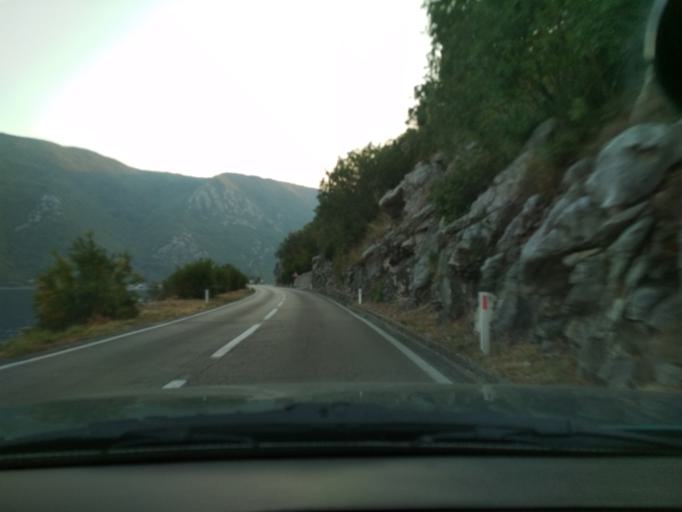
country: ME
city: Lipci
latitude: 42.5023
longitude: 18.6647
